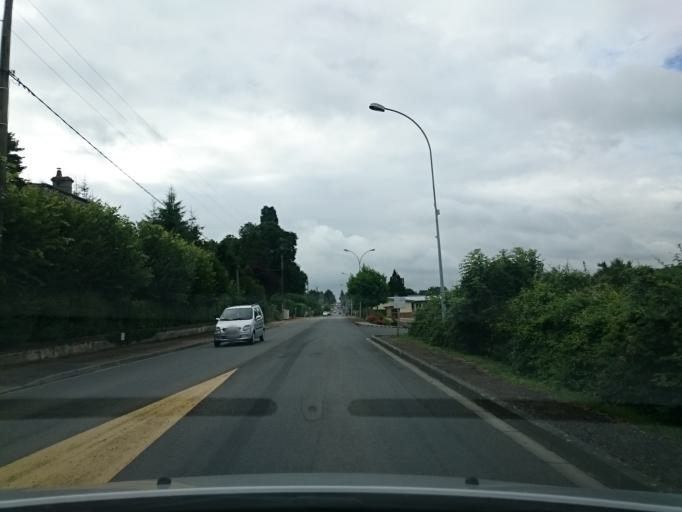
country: FR
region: Lower Normandy
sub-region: Departement du Calvados
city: La Vespiere
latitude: 49.0665
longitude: 0.3347
